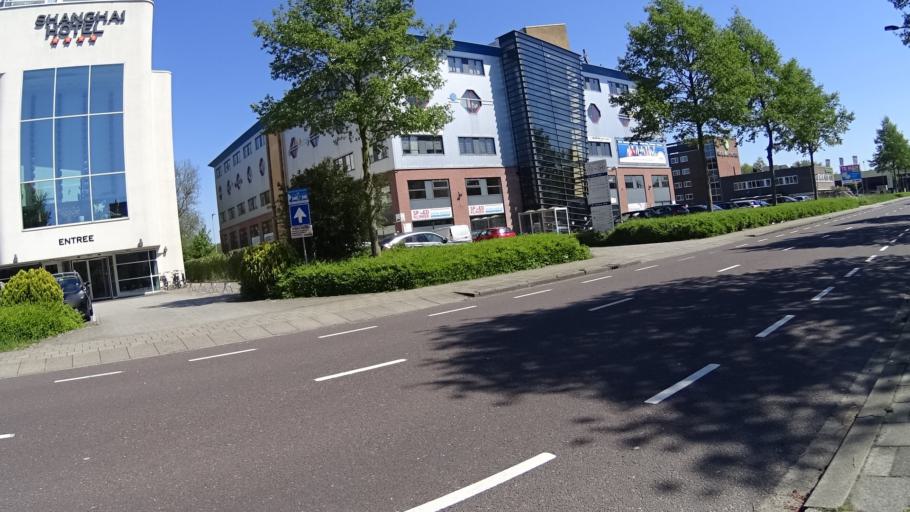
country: NL
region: South Holland
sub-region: Gemeente Den Haag
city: Ypenburg
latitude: 52.0256
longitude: 4.3637
